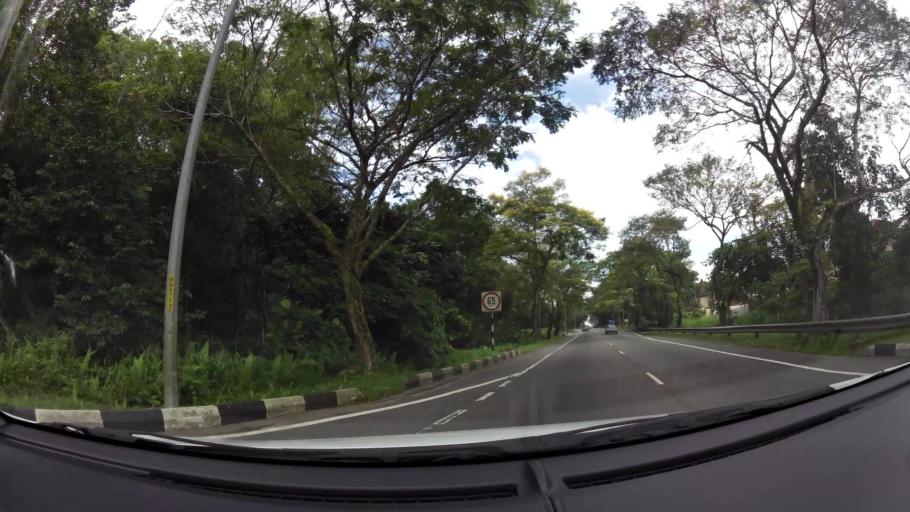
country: BN
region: Brunei and Muara
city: Bandar Seri Begawan
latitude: 4.8736
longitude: 114.8997
